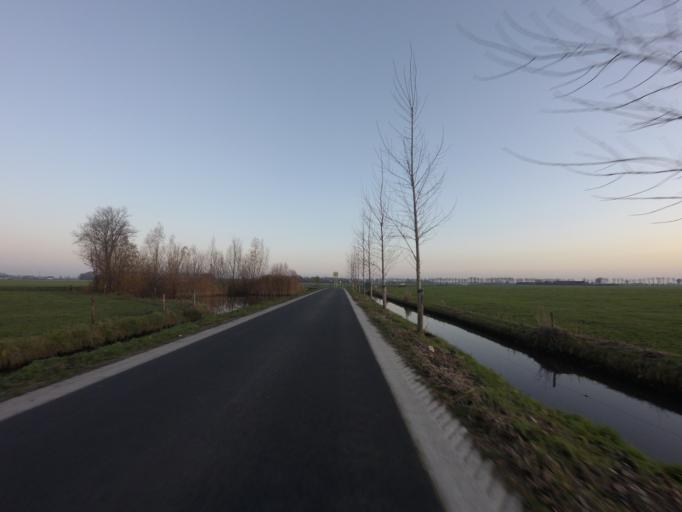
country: NL
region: Gelderland
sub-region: Gemeente Maasdriel
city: Hedel
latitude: 51.7716
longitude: 5.2388
